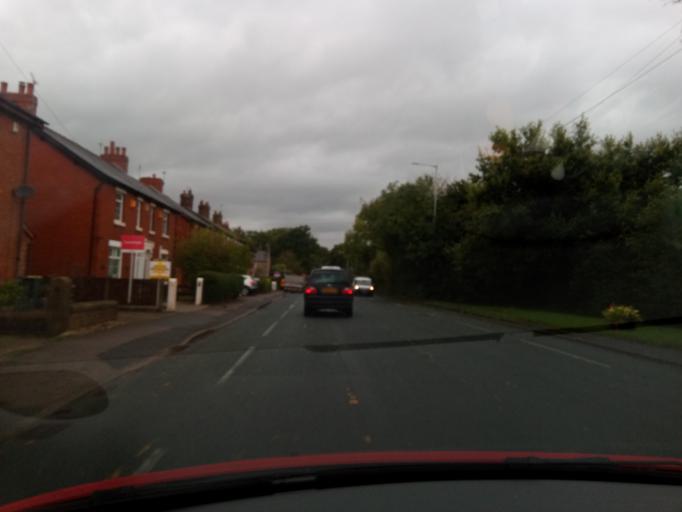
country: GB
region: England
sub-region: Lancashire
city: Catterall
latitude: 53.8386
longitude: -2.7397
